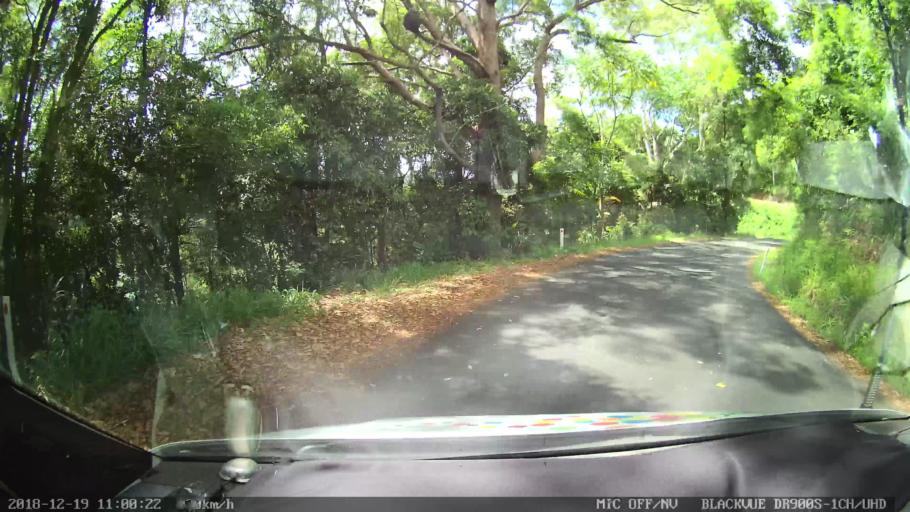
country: AU
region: New South Wales
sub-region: Lismore Municipality
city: Nimbin
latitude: -28.6015
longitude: 153.2639
